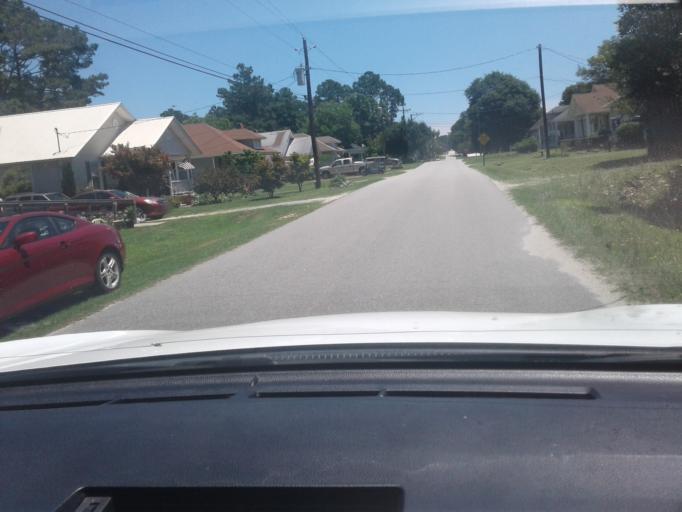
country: US
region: North Carolina
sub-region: Harnett County
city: Erwin
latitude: 35.3249
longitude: -78.6808
